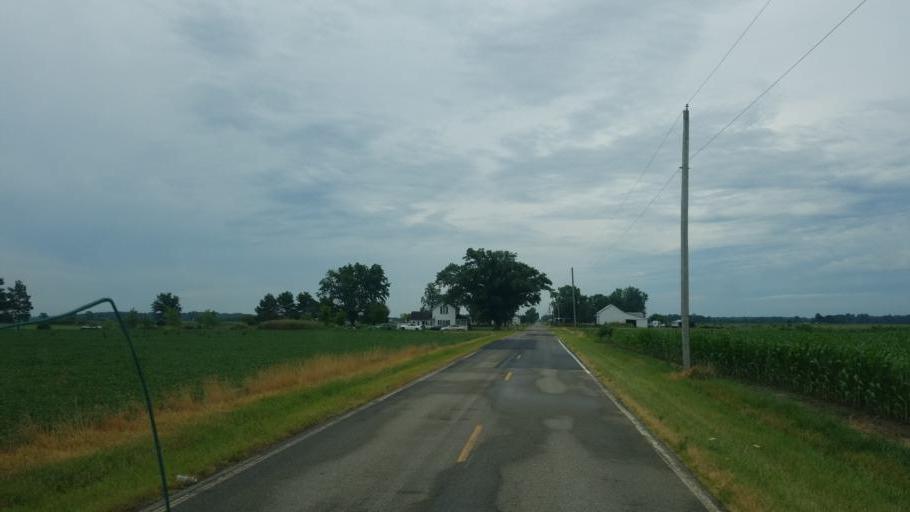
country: US
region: Ohio
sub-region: Defiance County
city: Hicksville
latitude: 41.2787
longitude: -84.6895
